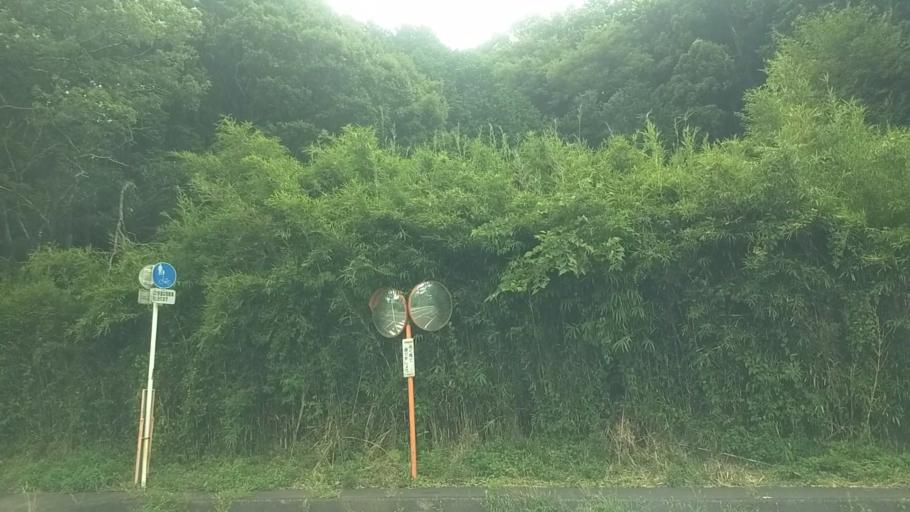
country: JP
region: Chiba
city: Kawaguchi
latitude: 35.2634
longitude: 140.0581
